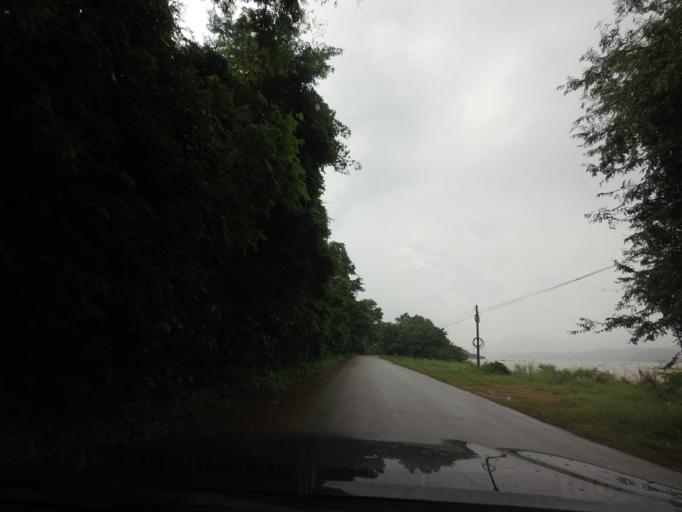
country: TH
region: Loei
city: Pak Chom
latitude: 18.1179
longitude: 101.9935
